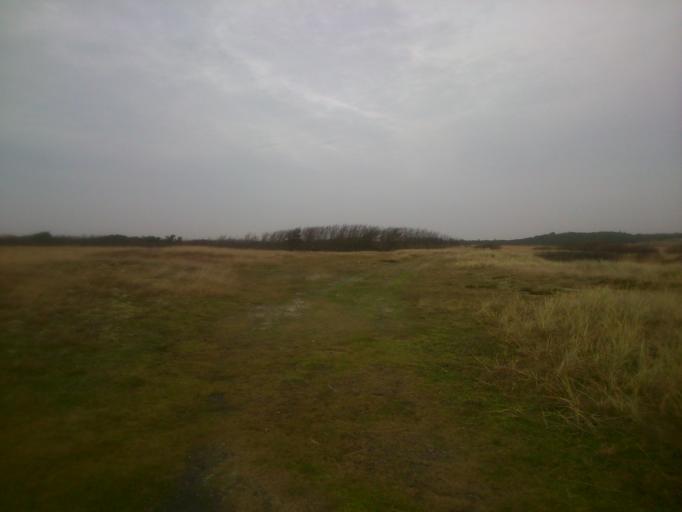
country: DK
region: Central Jutland
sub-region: Ringkobing-Skjern Kommune
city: Hvide Sande
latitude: 55.8190
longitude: 8.1832
